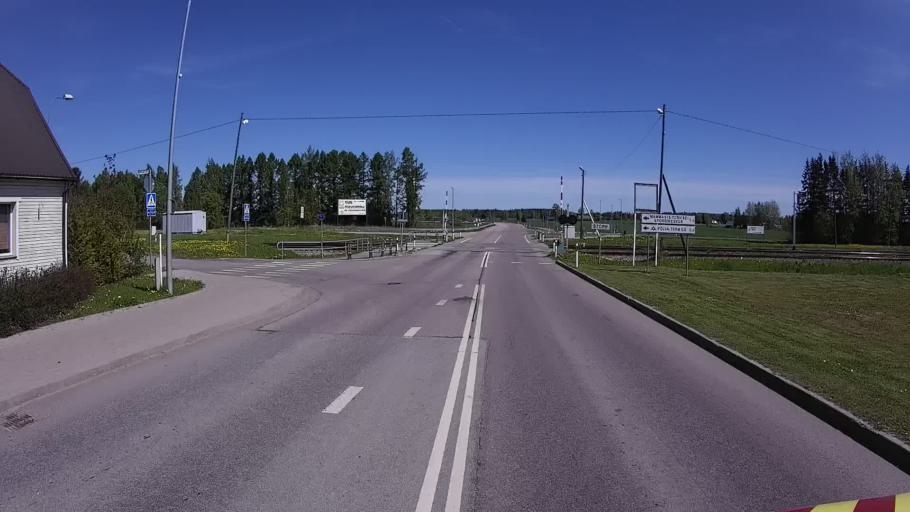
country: EE
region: Polvamaa
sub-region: Polva linn
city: Polva
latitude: 58.0712
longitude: 27.0855
